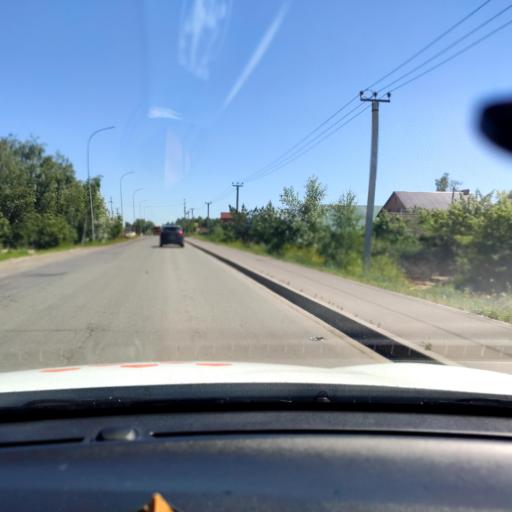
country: RU
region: Tatarstan
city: Stolbishchi
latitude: 55.6965
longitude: 49.1930
